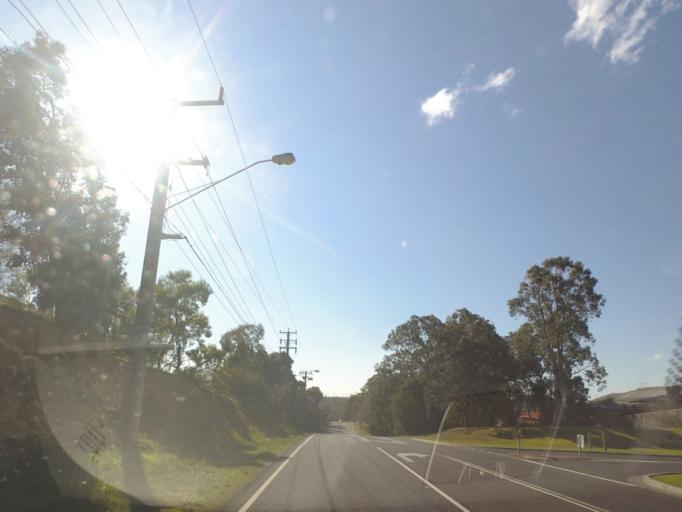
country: AU
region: Victoria
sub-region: Manningham
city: Donvale
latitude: -37.7733
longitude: 145.1833
